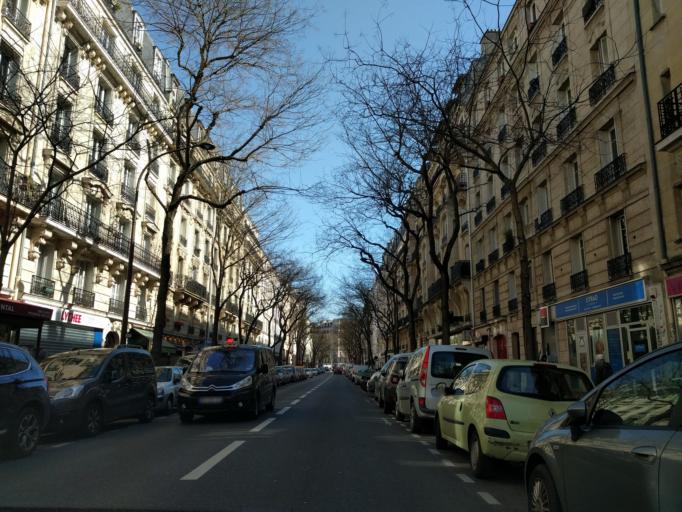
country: FR
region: Ile-de-France
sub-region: Departement du Val-de-Marne
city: Saint-Mande
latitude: 48.8350
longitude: 2.4013
